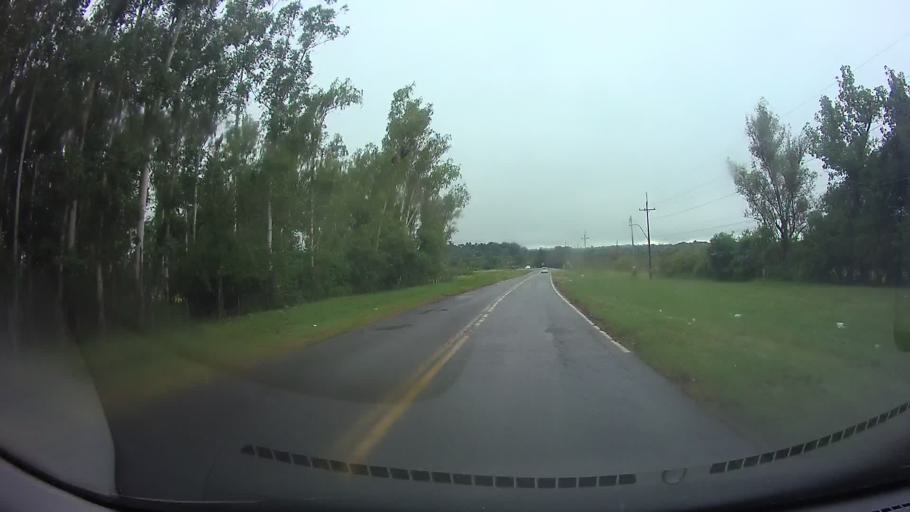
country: PY
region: Central
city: Ita
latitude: -25.5155
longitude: -57.3544
